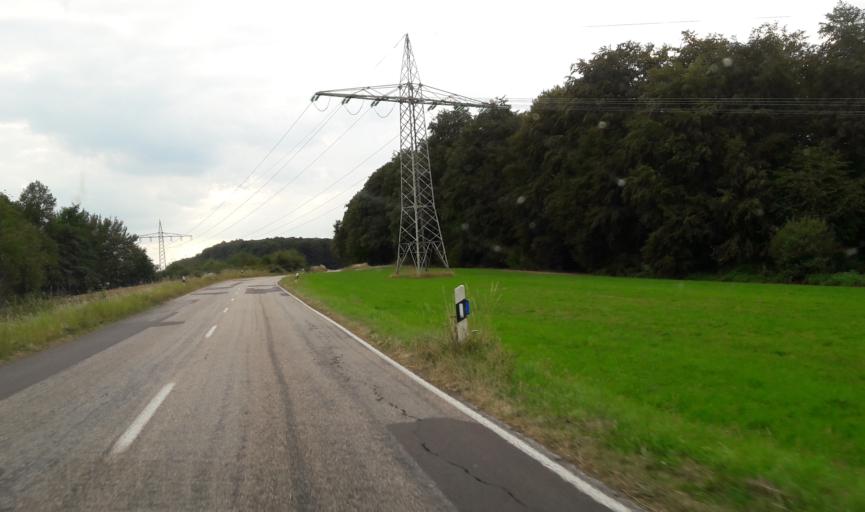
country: DE
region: Saarland
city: Tholey
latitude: 49.4570
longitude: 7.0203
